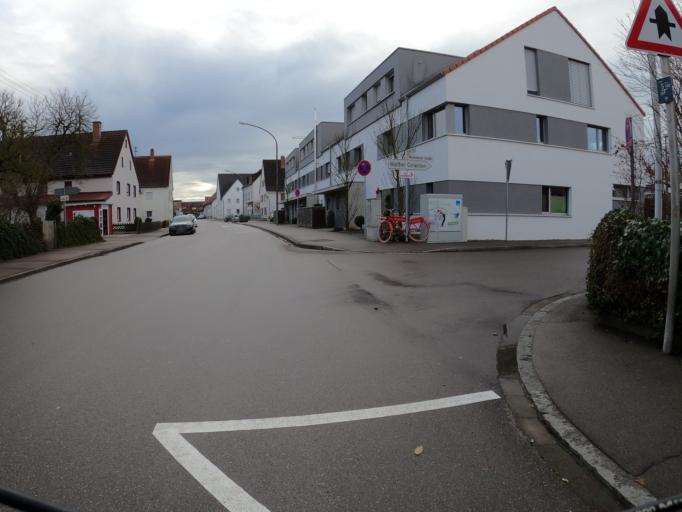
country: DE
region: Bavaria
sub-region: Swabia
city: Holzheim
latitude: 48.4156
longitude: 10.0677
